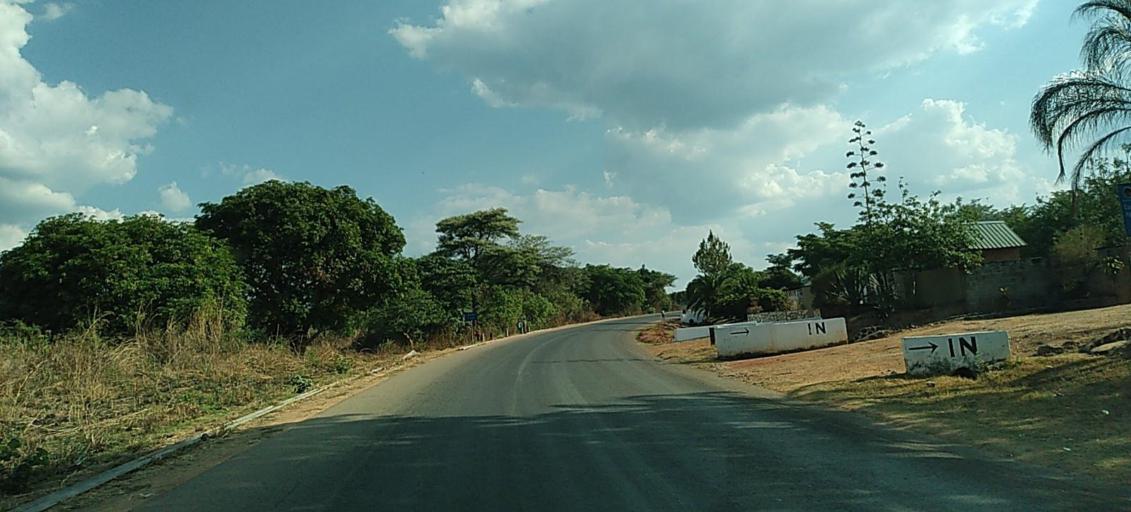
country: ZM
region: Copperbelt
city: Luanshya
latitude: -13.3483
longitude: 28.4207
